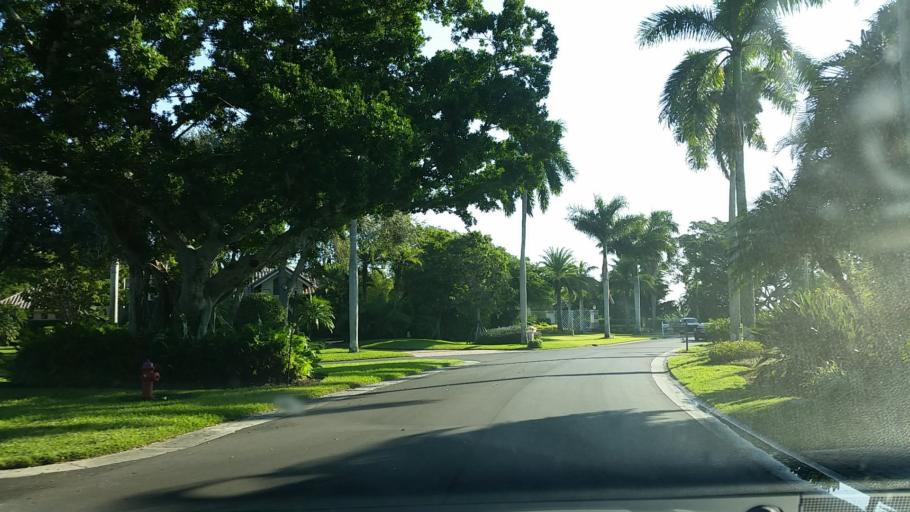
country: US
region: Florida
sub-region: Collier County
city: Naples
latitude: 26.1025
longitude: -81.7898
